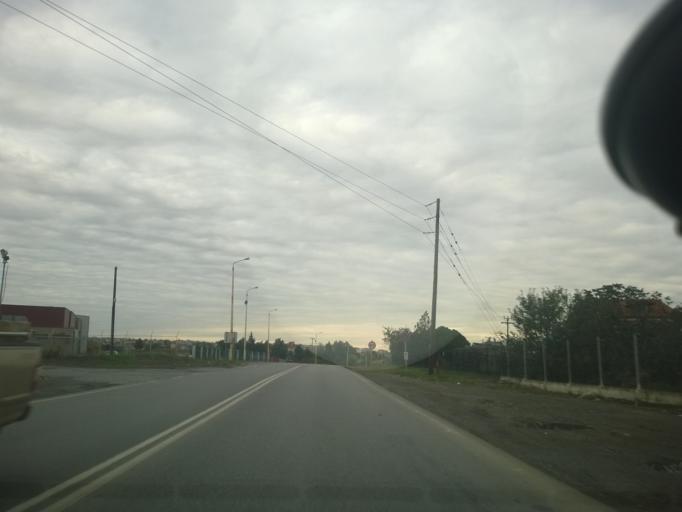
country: GR
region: Central Macedonia
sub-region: Nomos Pellis
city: Giannitsa
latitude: 40.7838
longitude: 22.3951
